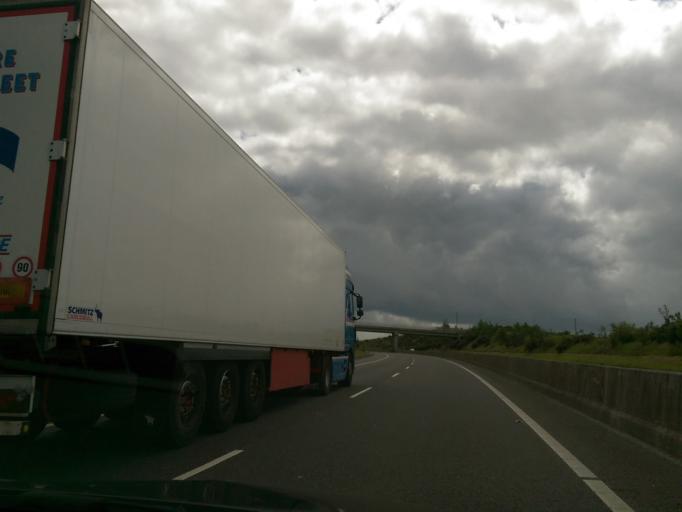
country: IE
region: Munster
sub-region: County Cork
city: Mitchelstown
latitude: 52.2239
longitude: -8.2877
